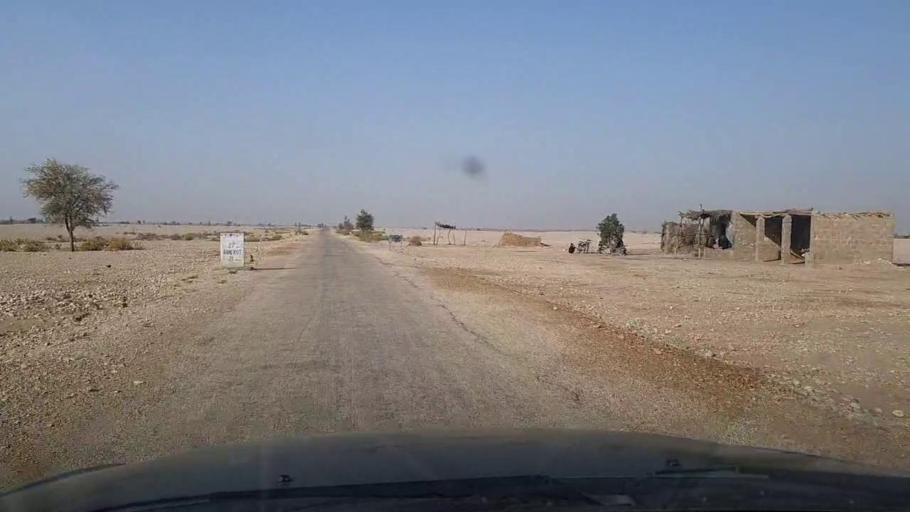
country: PK
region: Sindh
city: Sann
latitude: 25.9992
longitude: 68.0763
